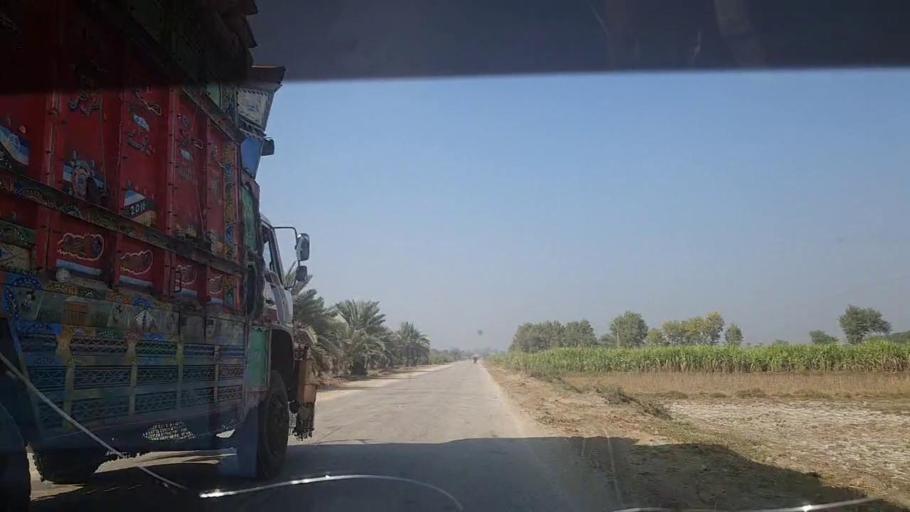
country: PK
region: Sindh
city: Kot Diji
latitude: 27.4212
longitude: 68.6604
